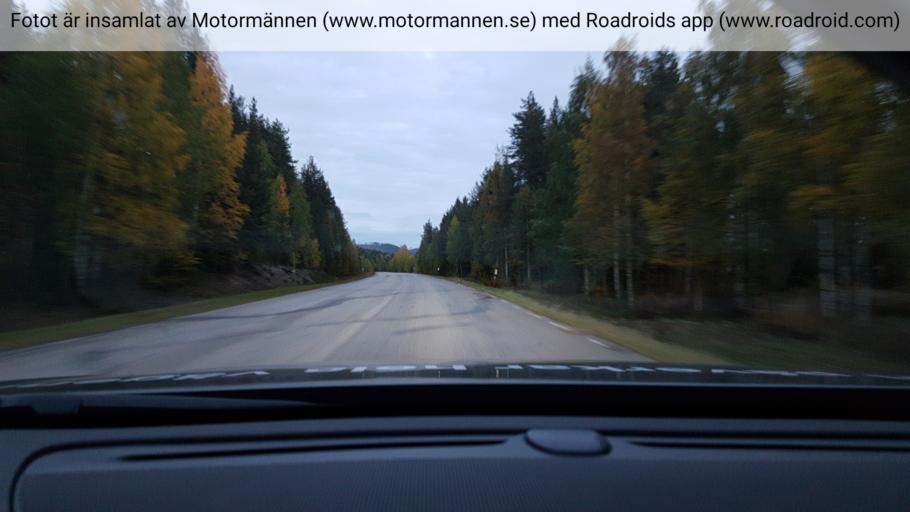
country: SE
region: Norrbotten
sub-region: Alvsbyns Kommun
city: AElvsbyn
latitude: 65.8350
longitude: 20.5242
